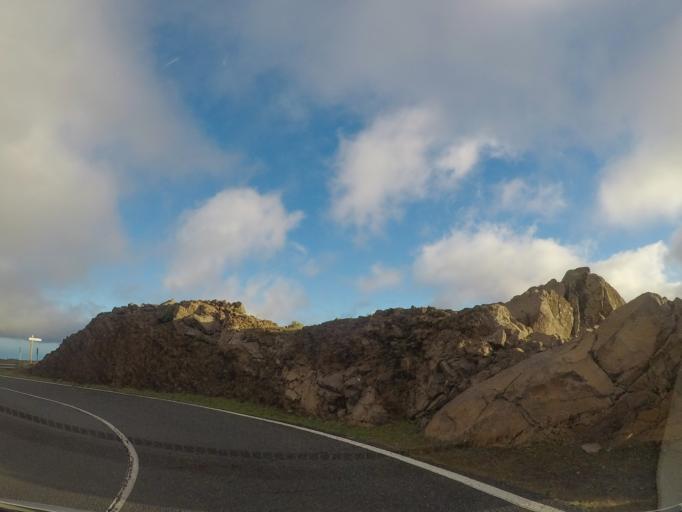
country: ES
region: Canary Islands
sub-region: Provincia de Santa Cruz de Tenerife
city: Alajero
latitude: 28.0869
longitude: -17.2572
